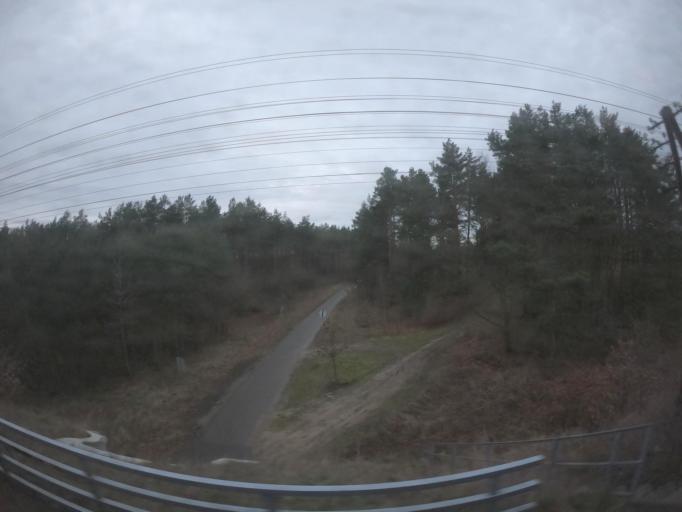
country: PL
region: West Pomeranian Voivodeship
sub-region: Powiat szczecinecki
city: Lubowo
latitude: 53.6215
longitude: 16.4525
